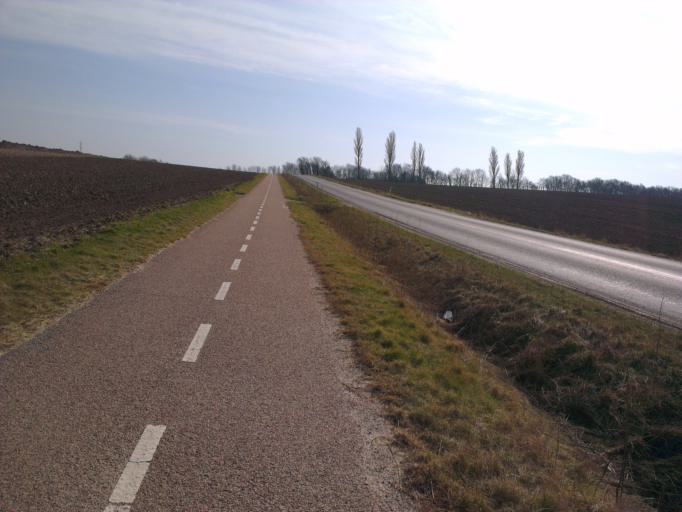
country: DK
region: Capital Region
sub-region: Frederikssund Kommune
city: Skibby
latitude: 55.8009
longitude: 11.9017
